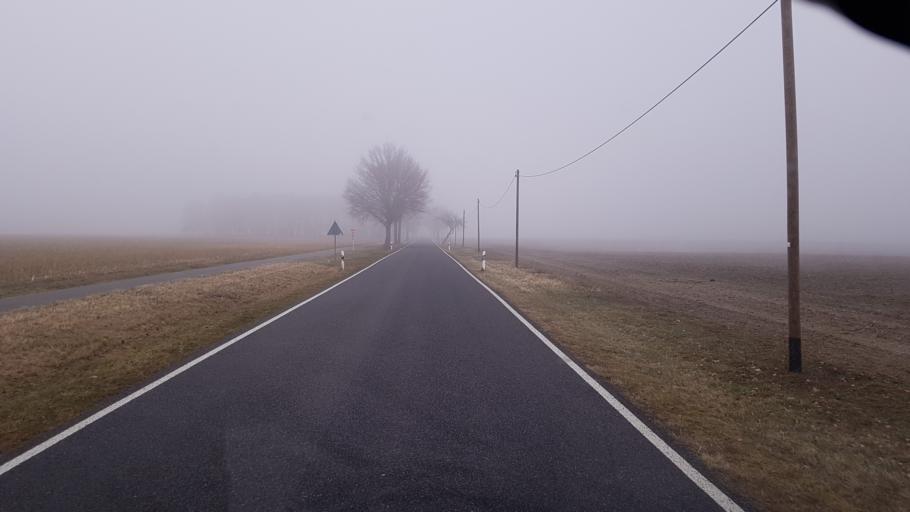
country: DE
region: Saxony-Anhalt
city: Holzdorf
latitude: 51.8516
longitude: 13.2115
